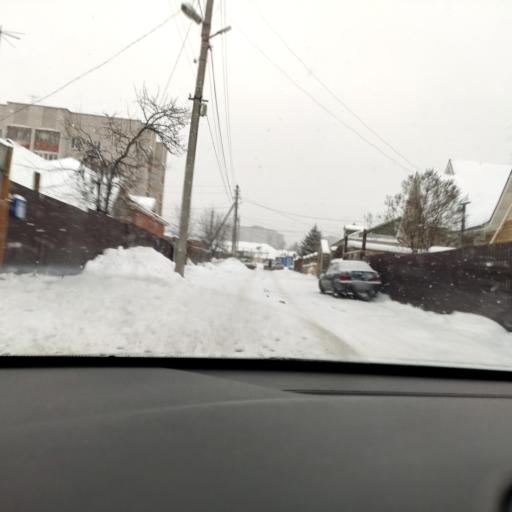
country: RU
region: Tatarstan
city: Vysokaya Gora
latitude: 55.8640
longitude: 49.2311
